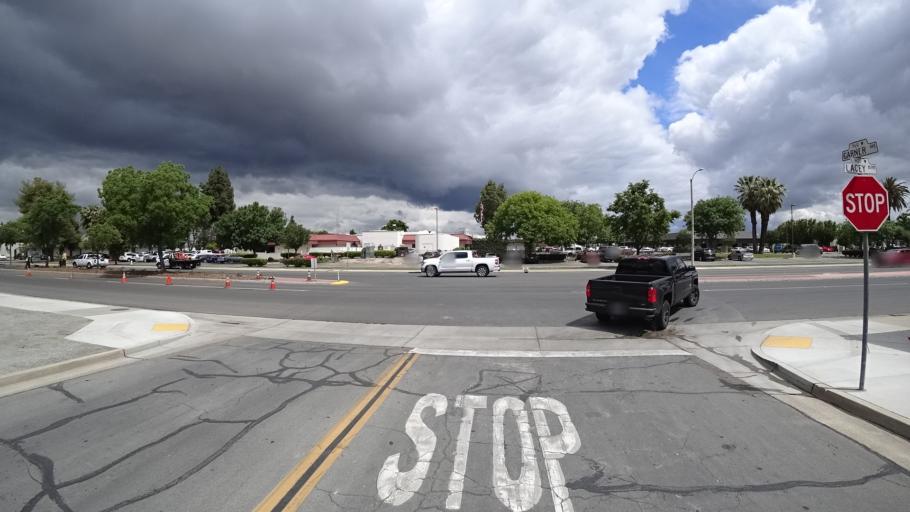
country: US
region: California
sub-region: Kings County
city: Hanford
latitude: 36.3278
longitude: -119.6593
